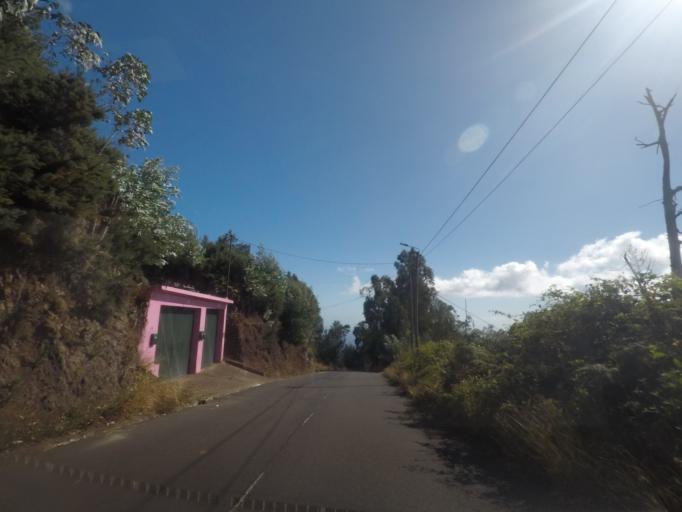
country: PT
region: Madeira
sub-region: Ribeira Brava
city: Campanario
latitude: 32.6855
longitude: -17.0217
